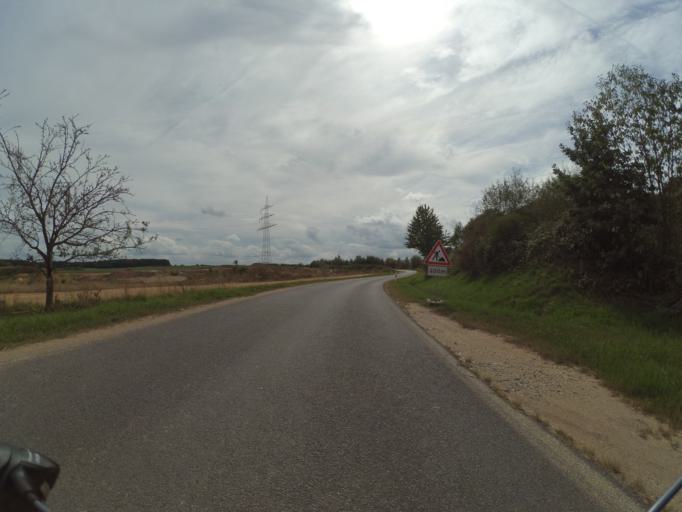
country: DE
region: Rheinland-Pfalz
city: Gladbach
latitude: 49.9267
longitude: 6.7745
